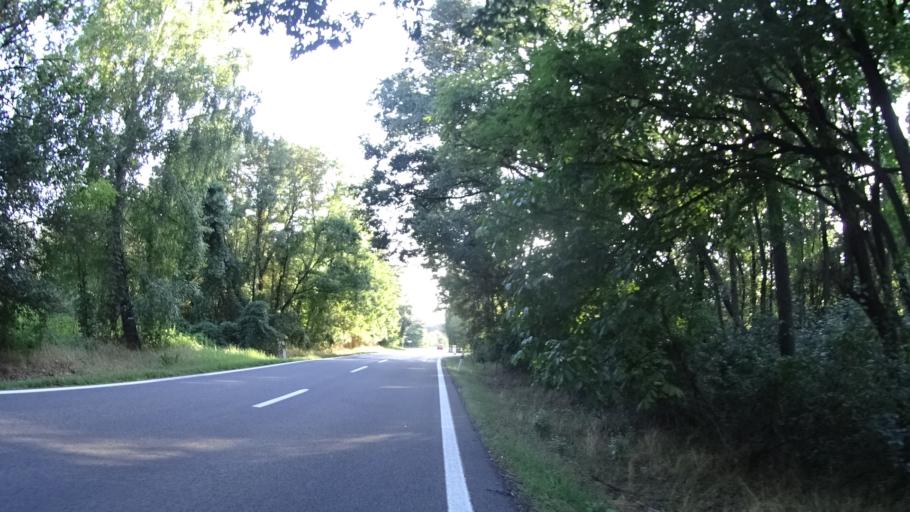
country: HU
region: Komarom-Esztergom
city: Nyergesujfalu
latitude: 47.7764
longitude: 18.5653
